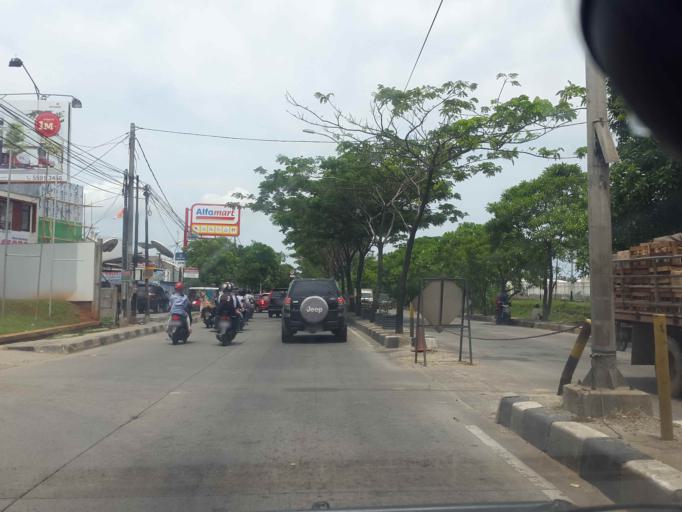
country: ID
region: Banten
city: Tangerang
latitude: -6.1443
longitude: 106.6327
